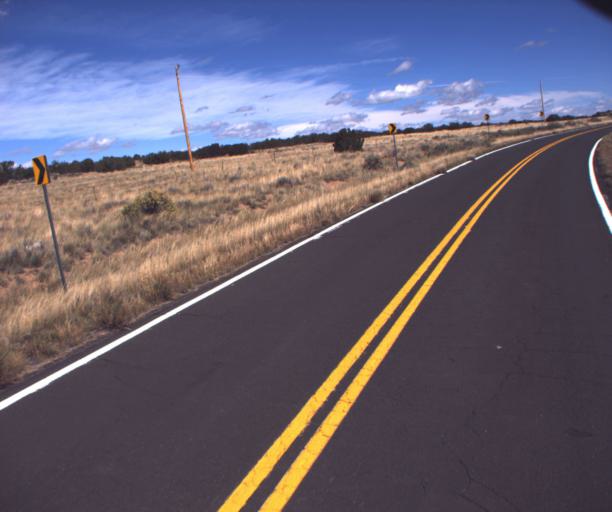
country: US
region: Arizona
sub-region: Apache County
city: Houck
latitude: 34.9299
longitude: -109.1985
